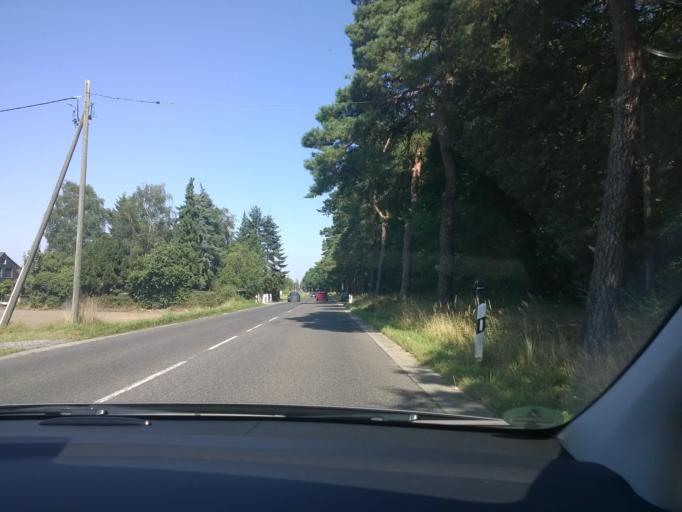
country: DE
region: North Rhine-Westphalia
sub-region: Regierungsbezirk Koln
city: Rath
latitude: 50.9359
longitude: 7.0900
